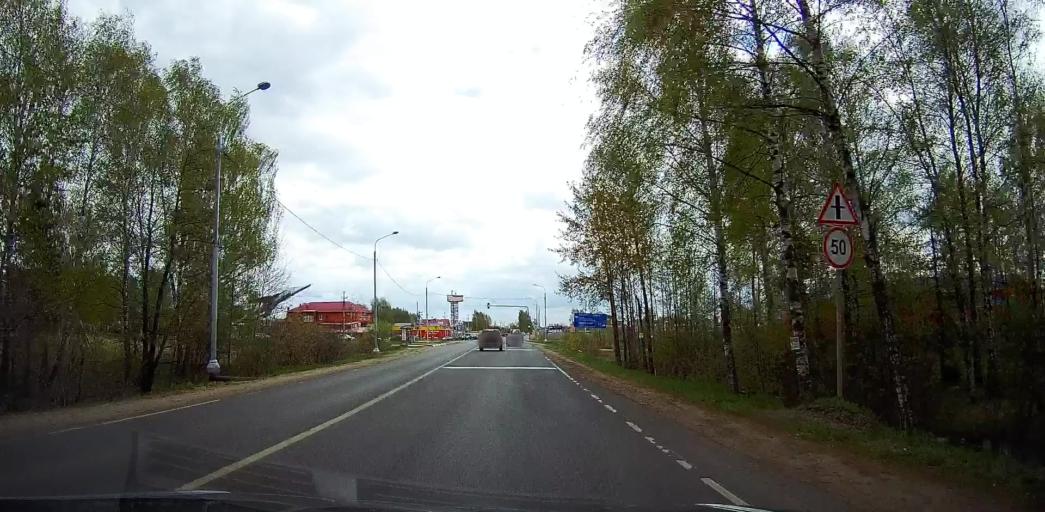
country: RU
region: Moskovskaya
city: Beloozerskiy
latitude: 55.4529
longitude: 38.4351
